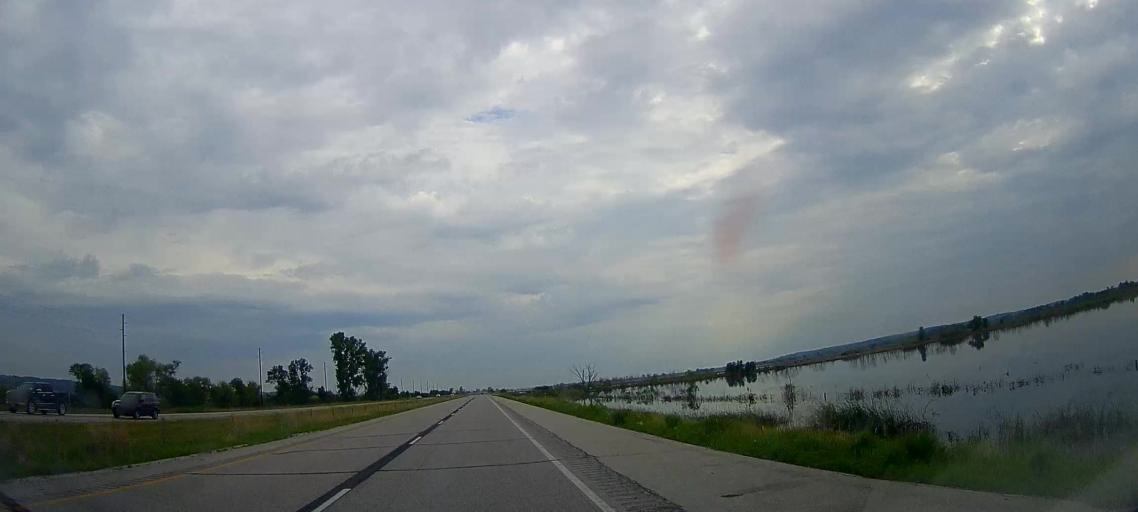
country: US
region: Iowa
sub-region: Harrison County
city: Missouri Valley
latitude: 41.4594
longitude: -95.8997
